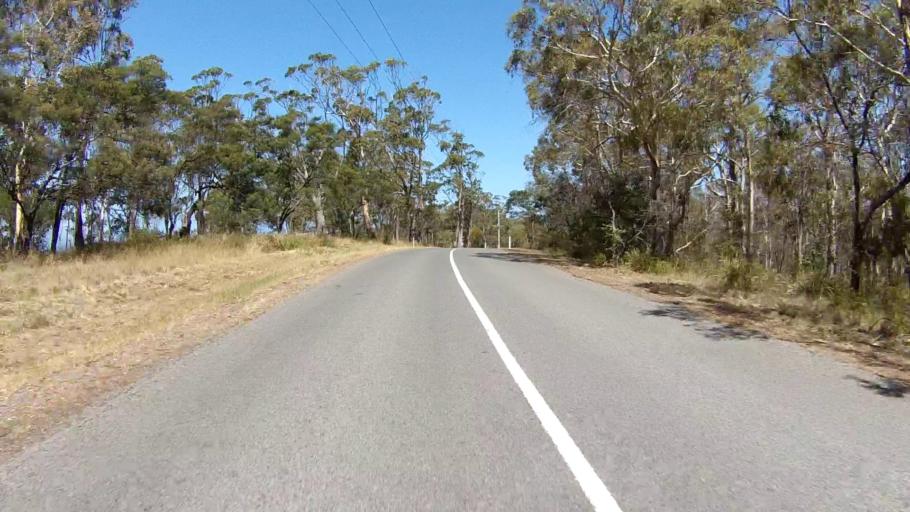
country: AU
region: Tasmania
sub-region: Clarence
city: Sandford
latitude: -43.0162
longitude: 147.4818
